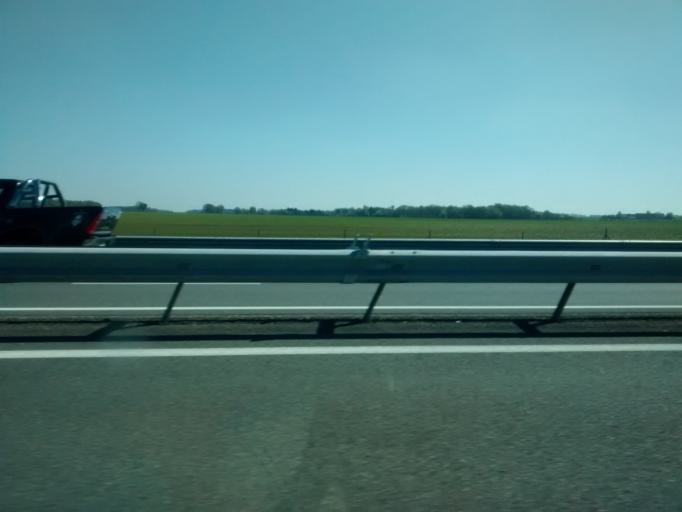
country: FR
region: Centre
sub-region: Departement du Cher
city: Levet
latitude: 46.9207
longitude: 2.4246
